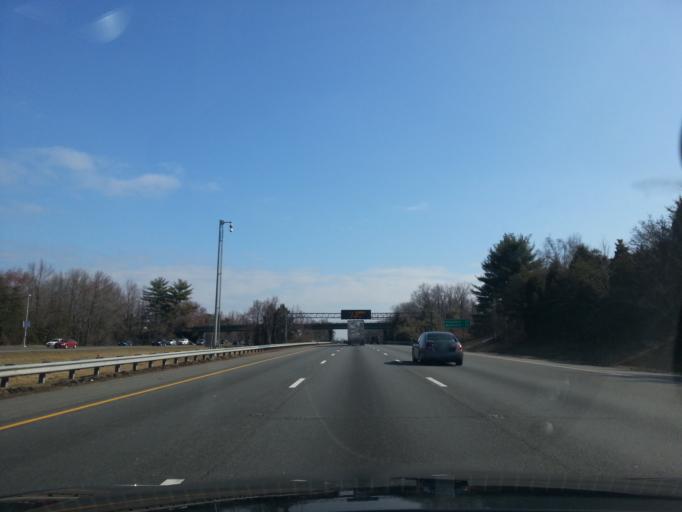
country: US
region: Virginia
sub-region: Stafford County
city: Falmouth
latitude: 38.3503
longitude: -77.4802
